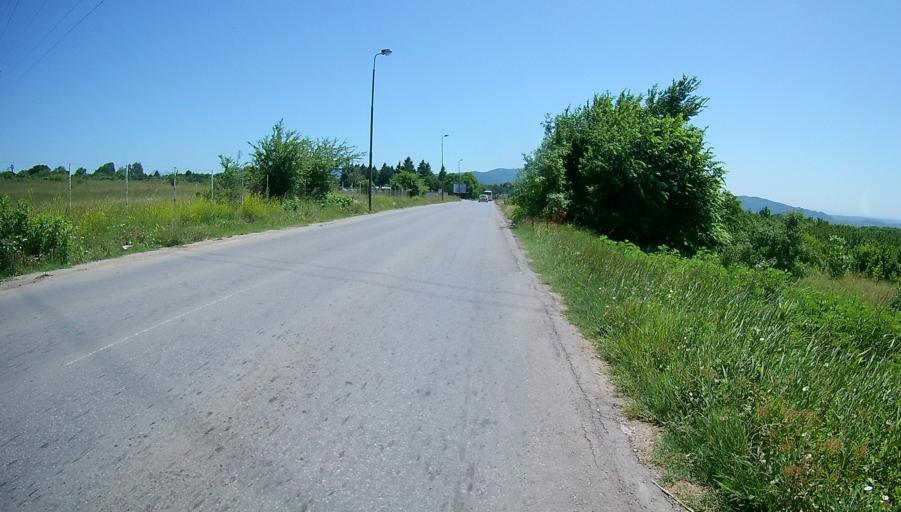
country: RS
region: Central Serbia
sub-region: Nisavski Okrug
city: Nis
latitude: 43.2968
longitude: 21.8788
